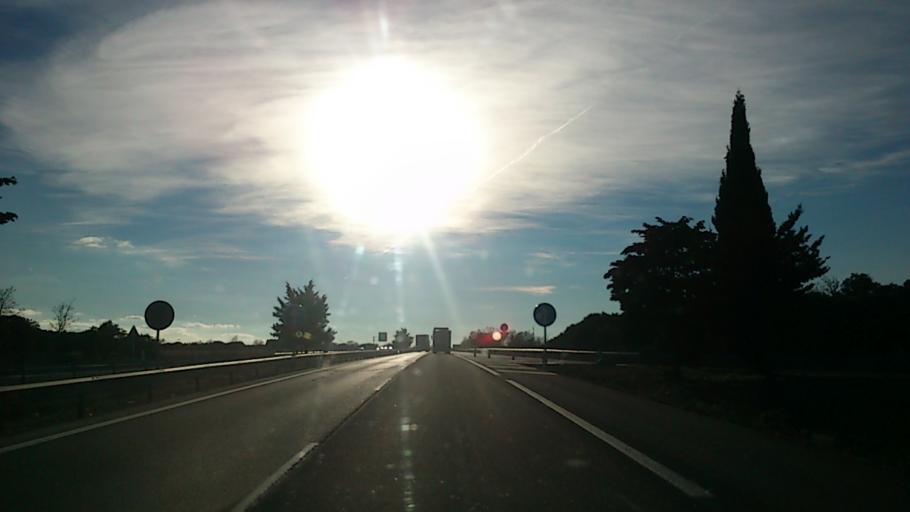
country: ES
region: Castille-La Mancha
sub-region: Provincia de Guadalajara
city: Mirabueno
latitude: 40.9118
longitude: -2.7392
